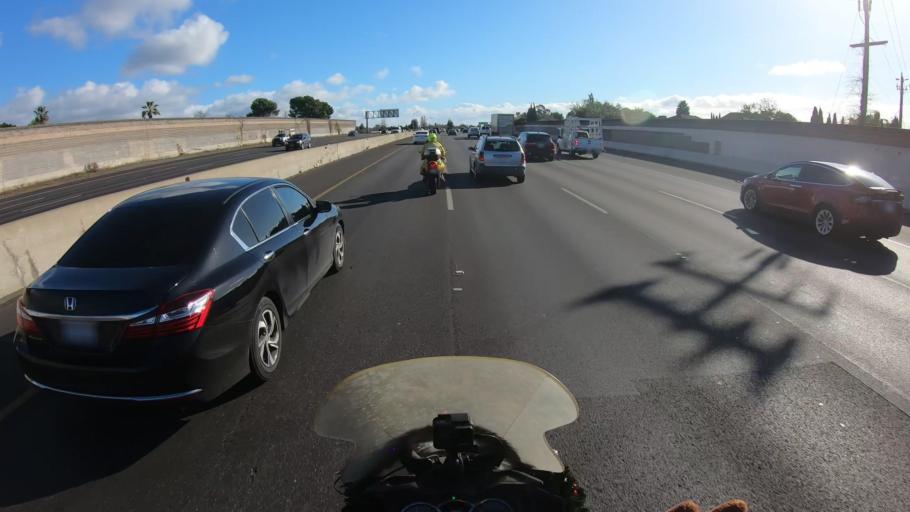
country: US
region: California
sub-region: Alameda County
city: Union City
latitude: 37.5843
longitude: -122.0568
